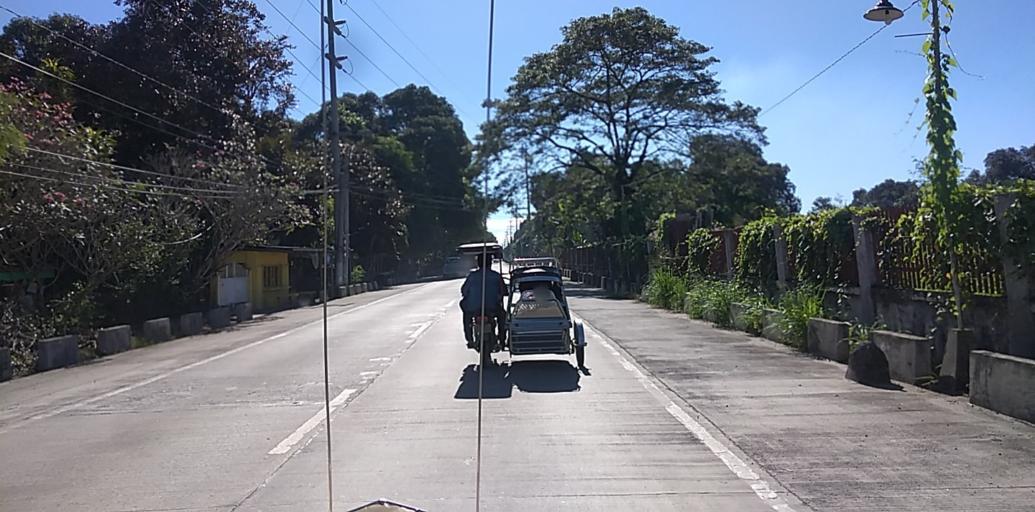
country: PH
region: Central Luzon
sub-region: Province of Pampanga
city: Santo Domingo
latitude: 15.0666
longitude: 120.7670
